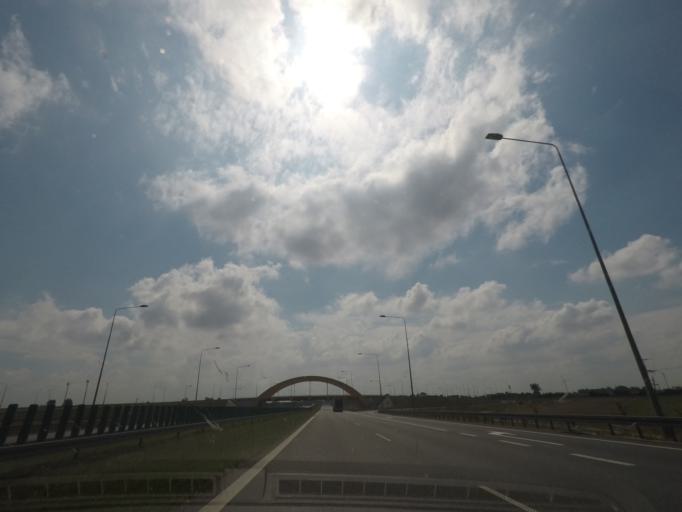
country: PL
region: Lodz Voivodeship
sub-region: Powiat kutnowski
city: Krzyzanow
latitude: 52.2264
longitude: 19.4632
